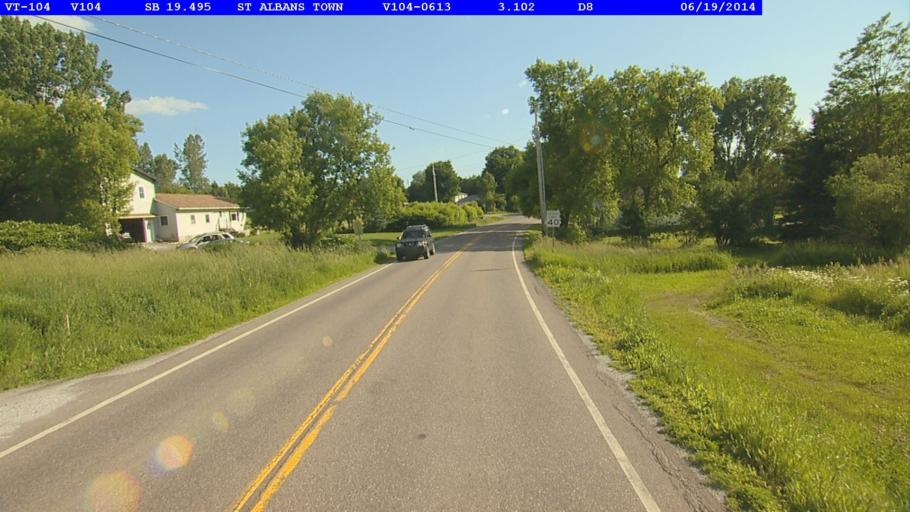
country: US
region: Vermont
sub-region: Franklin County
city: Saint Albans
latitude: 44.8153
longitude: -73.0608
